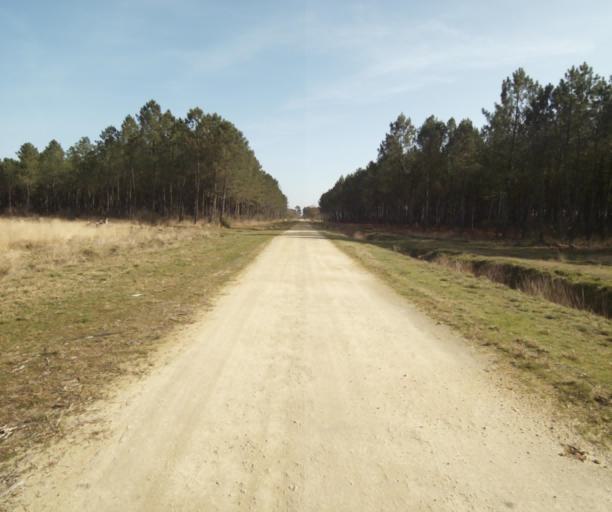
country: FR
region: Aquitaine
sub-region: Departement de la Gironde
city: Bazas
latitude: 44.2259
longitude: -0.2374
